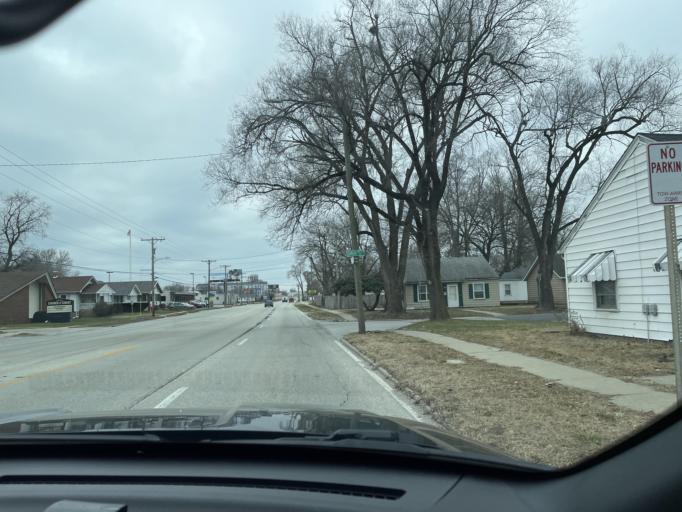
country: US
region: Illinois
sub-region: Sangamon County
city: Grandview
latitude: 39.8021
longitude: -89.6204
